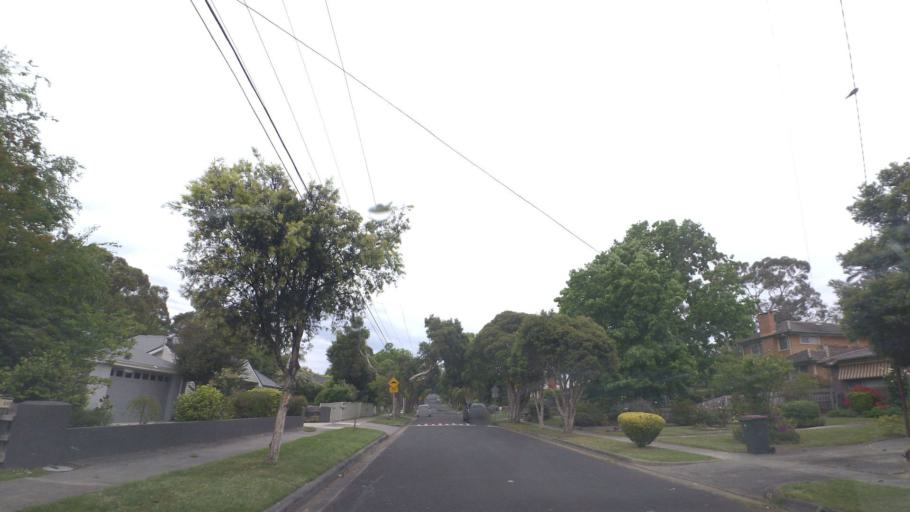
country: AU
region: Victoria
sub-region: Maroondah
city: Croydon North
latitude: -37.7898
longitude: 145.2982
